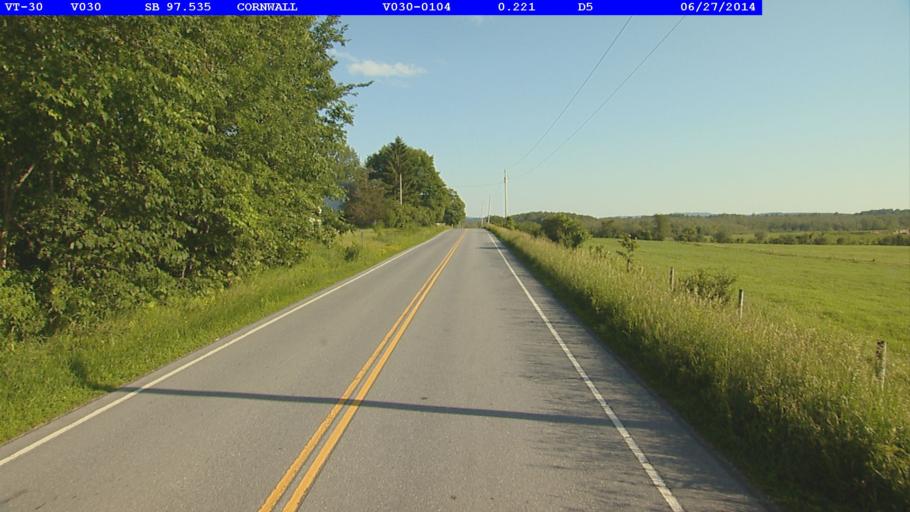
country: US
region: Vermont
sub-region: Addison County
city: Middlebury (village)
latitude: 43.9112
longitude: -73.2084
